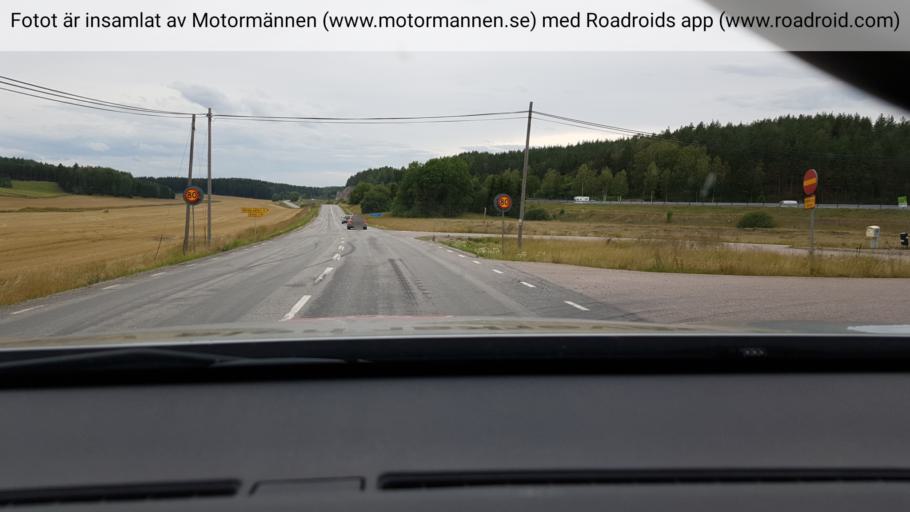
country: SE
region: Soedermanland
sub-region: Gnesta Kommun
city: Gnesta
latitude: 58.9018
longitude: 17.3110
